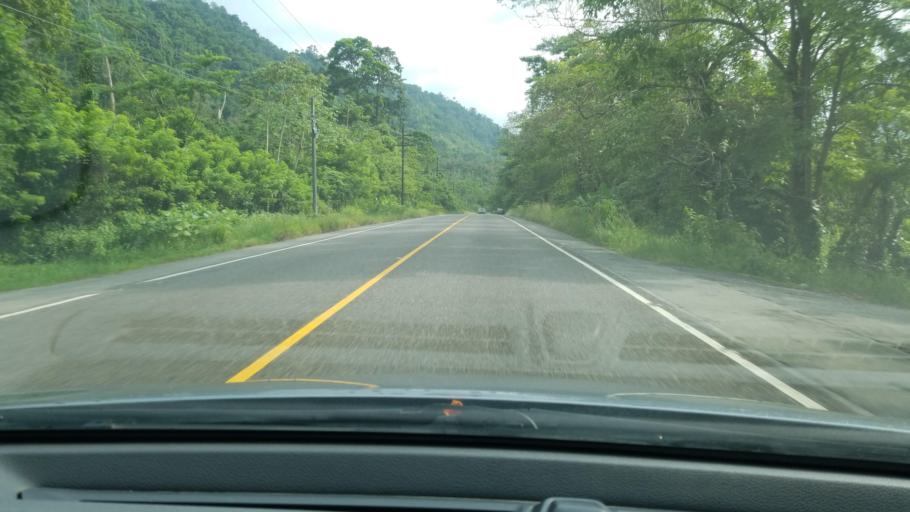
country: HN
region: Cortes
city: Potrerillos
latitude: 15.5994
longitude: -88.2979
